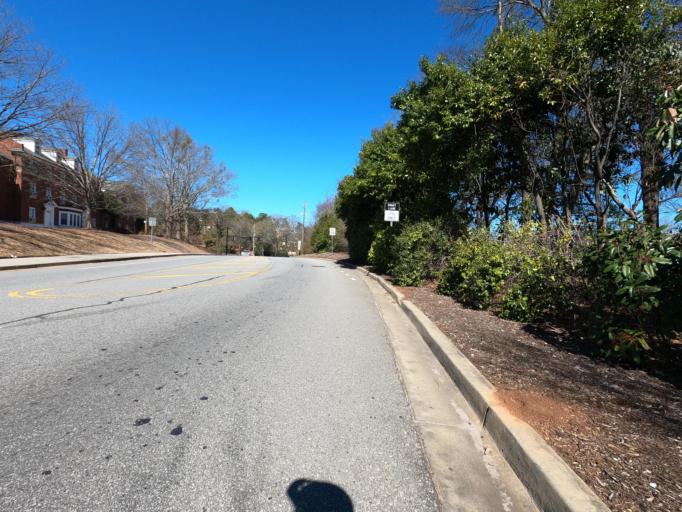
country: US
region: Georgia
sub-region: Clarke County
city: Athens
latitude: 33.9513
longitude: -83.3713
